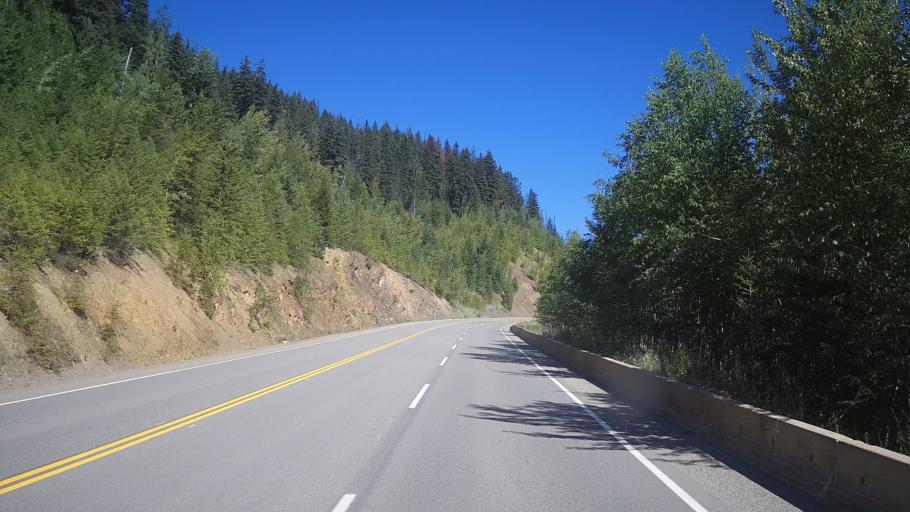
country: CA
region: British Columbia
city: Kamloops
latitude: 51.4878
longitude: -120.2671
